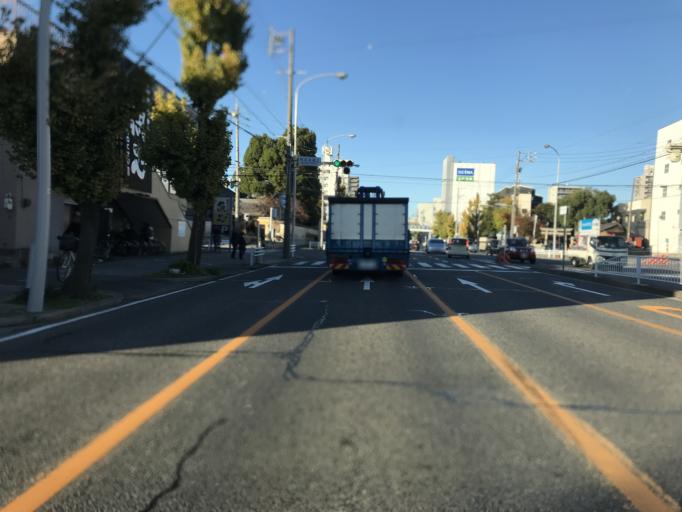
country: JP
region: Aichi
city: Nagoya-shi
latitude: 35.1719
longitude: 136.8728
